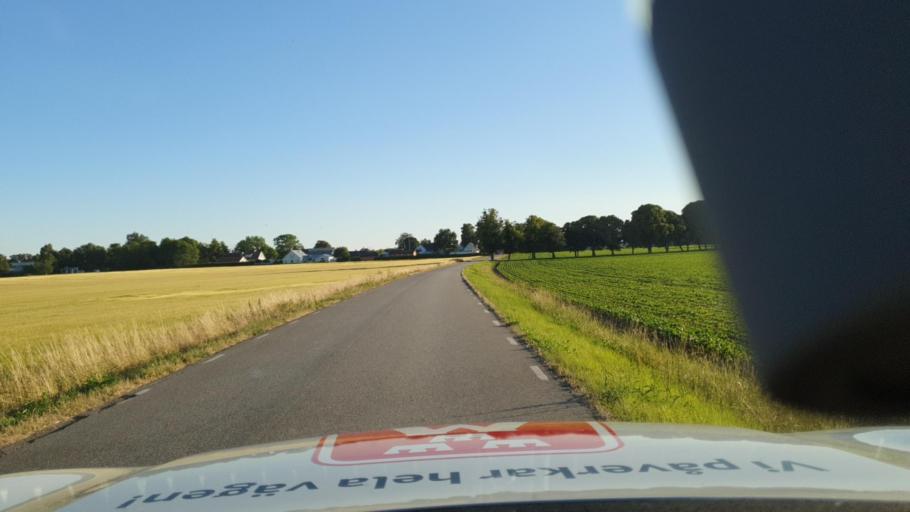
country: SE
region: Skane
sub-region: Lomma Kommun
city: Lomma
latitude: 55.7010
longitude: 13.0573
